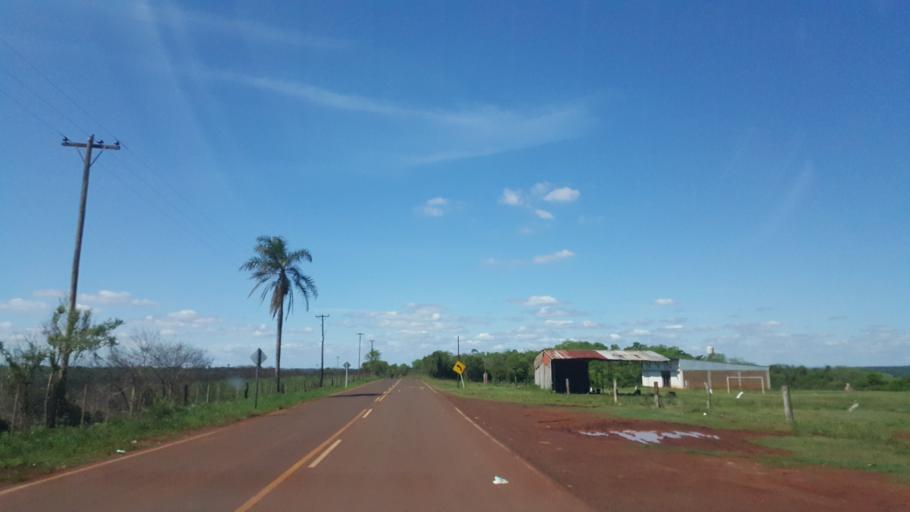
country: AR
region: Misiones
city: Garupa
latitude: -27.4984
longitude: -55.8442
